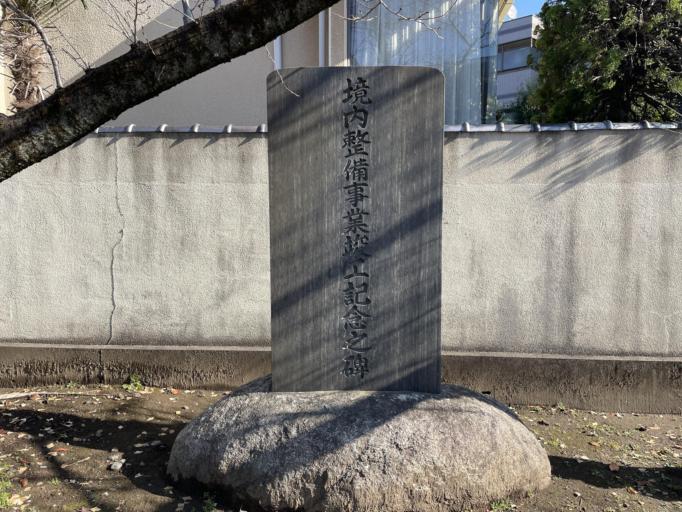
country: JP
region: Chiba
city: Matsudo
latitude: 35.7754
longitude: 139.8776
